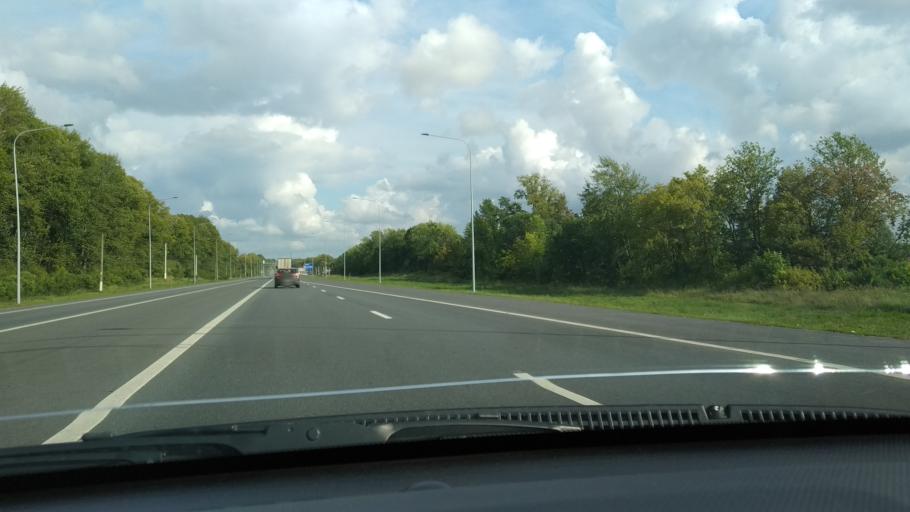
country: RU
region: Tatarstan
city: Stolbishchi
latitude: 55.6589
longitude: 49.3039
